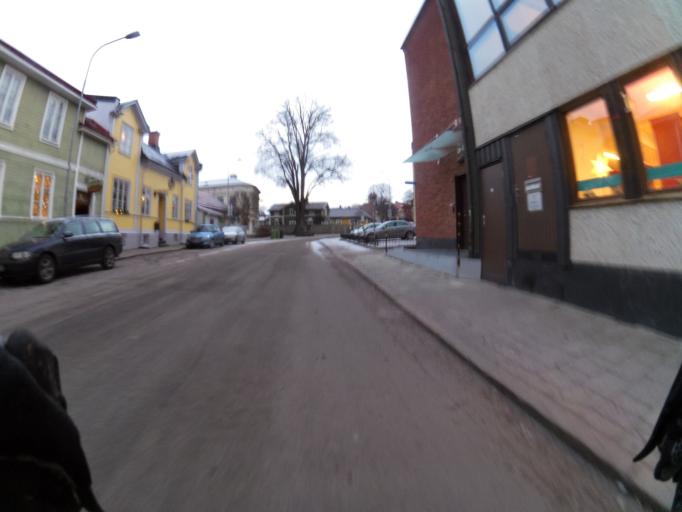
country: SE
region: Gaevleborg
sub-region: Gavle Kommun
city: Gavle
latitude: 60.6735
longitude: 17.1477
